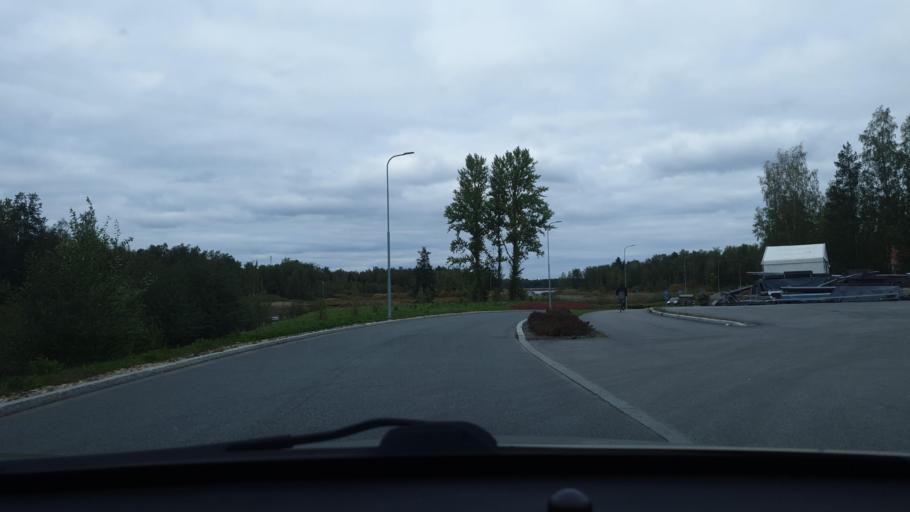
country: FI
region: Ostrobothnia
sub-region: Vaasa
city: Vaasa
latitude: 63.1178
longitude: 21.6202
